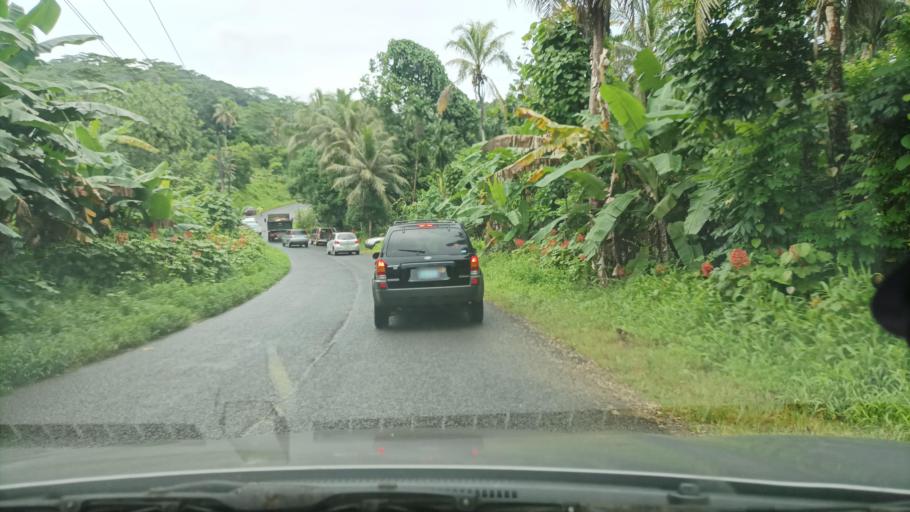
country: FM
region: Pohnpei
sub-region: Sokehs Municipality
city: Palikir - National Government Center
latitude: 6.8986
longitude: 158.1568
